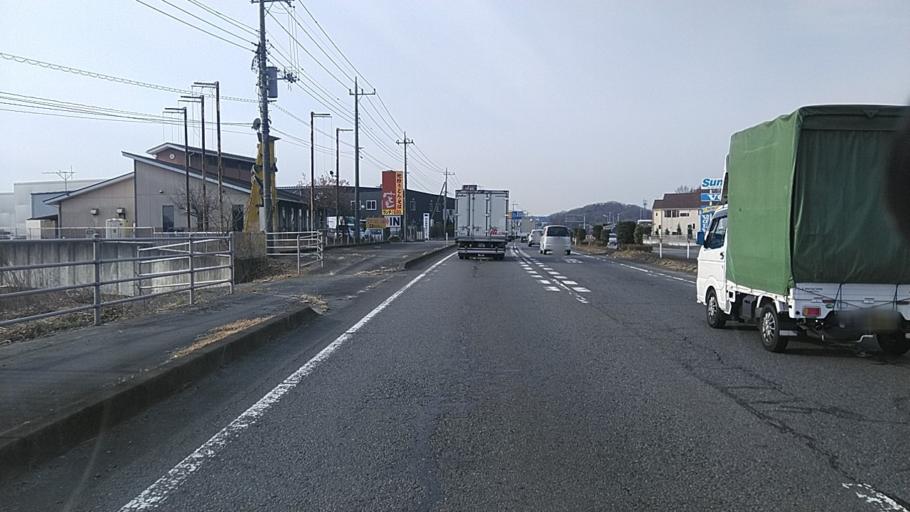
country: JP
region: Tochigi
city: Sano
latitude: 36.2983
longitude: 139.6303
